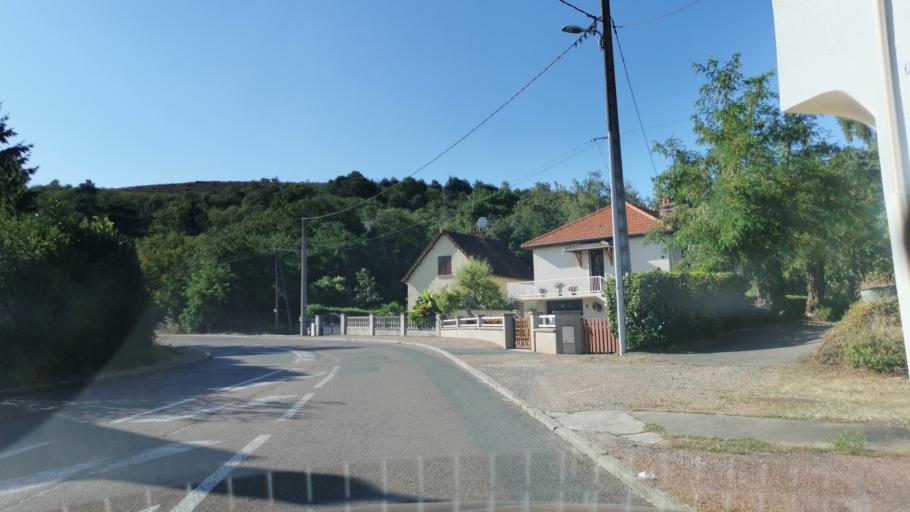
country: FR
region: Bourgogne
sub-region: Departement de Saone-et-Loire
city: Montcenis
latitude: 46.7983
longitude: 4.3999
